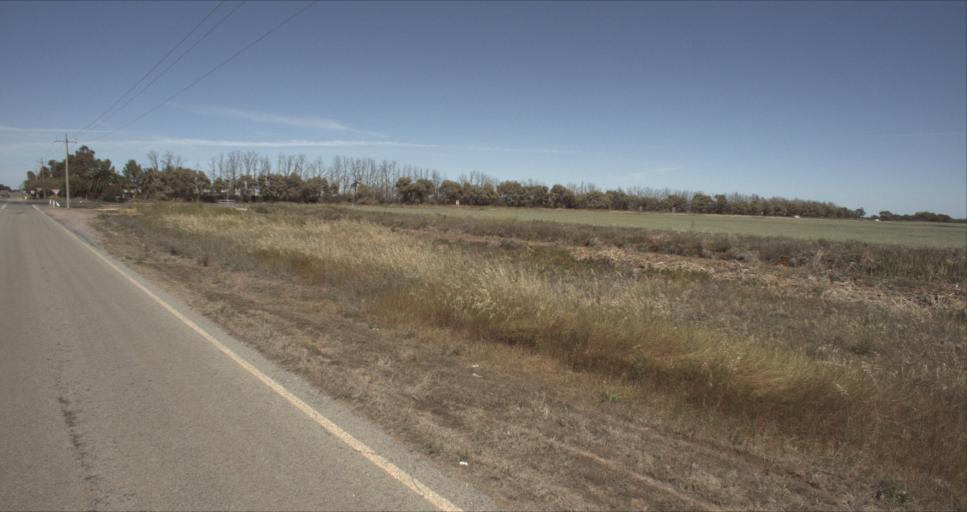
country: AU
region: New South Wales
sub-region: Leeton
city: Leeton
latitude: -34.5187
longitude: 146.2837
